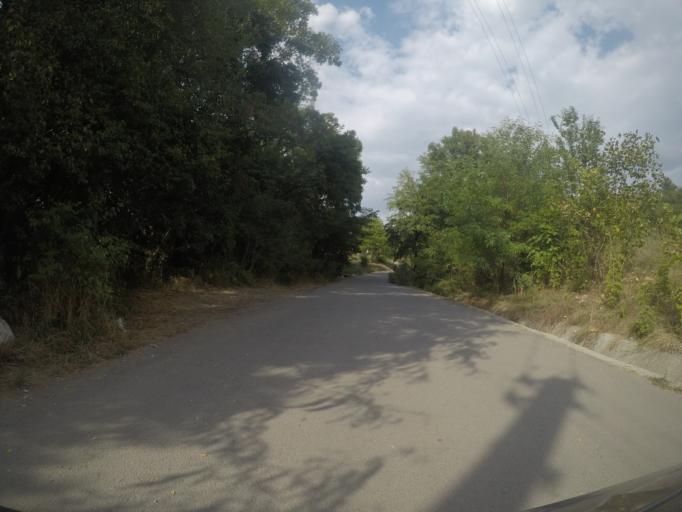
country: RO
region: Cluj
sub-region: Comuna Sandulesti
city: Sandulesti
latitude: 46.5623
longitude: 23.6912
